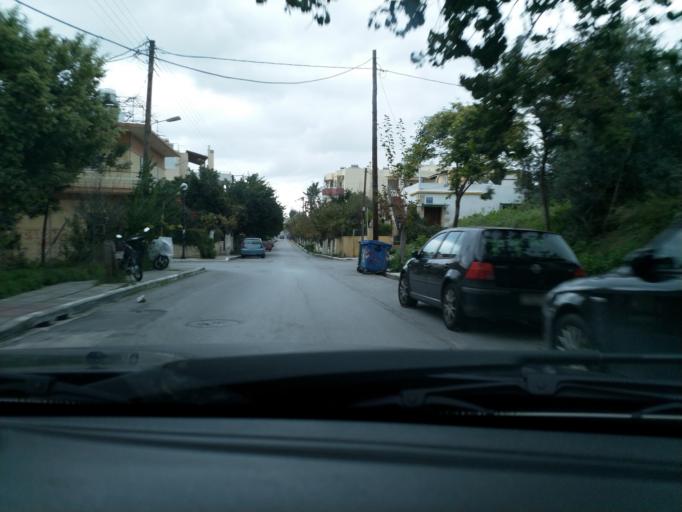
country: GR
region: Crete
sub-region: Nomos Chanias
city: Chania
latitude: 35.5107
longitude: 24.0357
